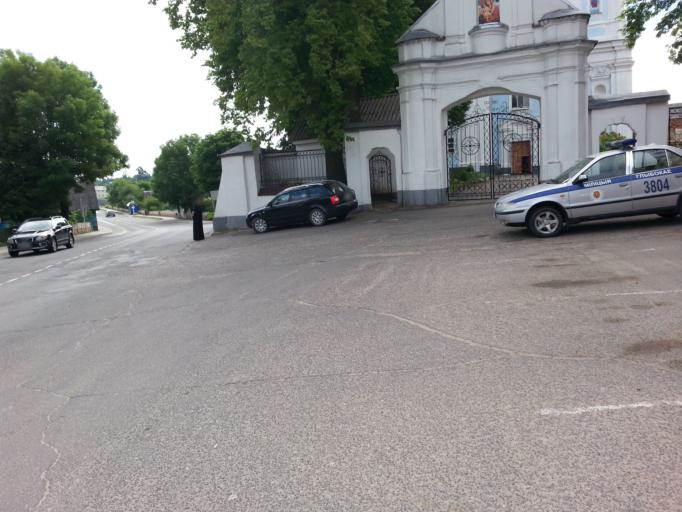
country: BY
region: Vitebsk
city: Hlybokaye
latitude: 55.1397
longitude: 27.6959
